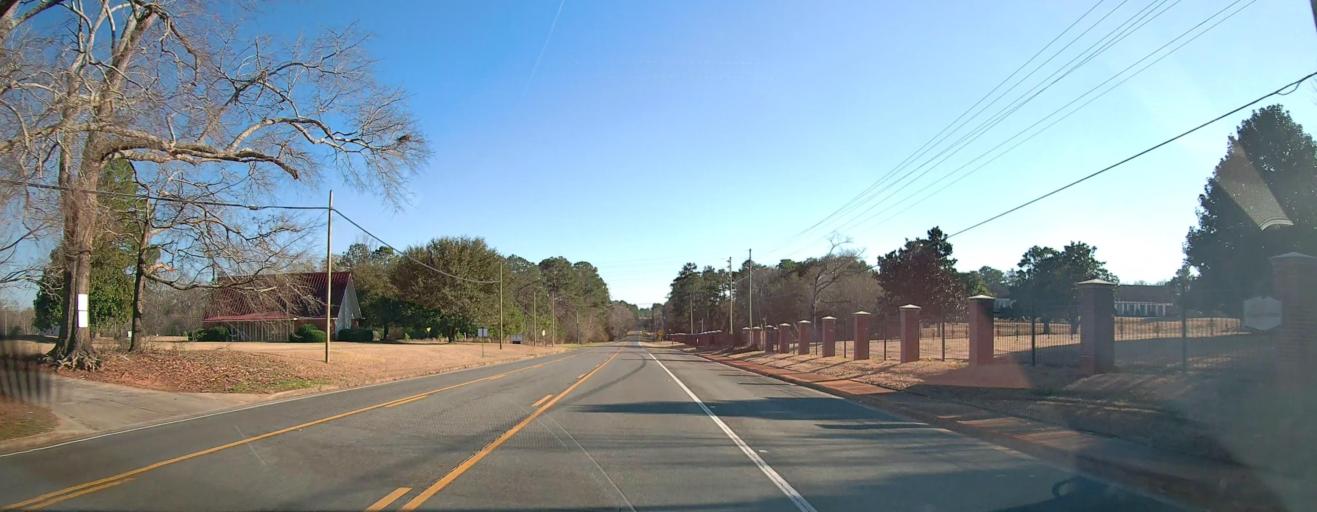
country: US
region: Georgia
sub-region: Sumter County
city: Americus
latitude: 32.0454
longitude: -84.2231
